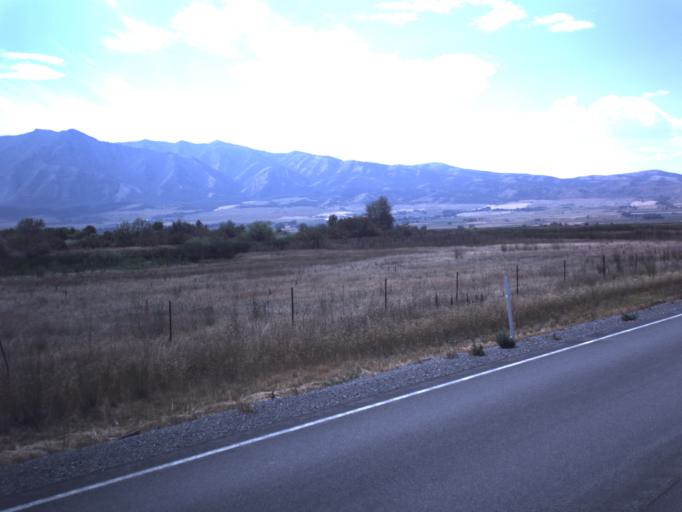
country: US
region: Utah
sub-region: Cache County
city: Benson
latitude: 41.7446
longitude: -111.9241
